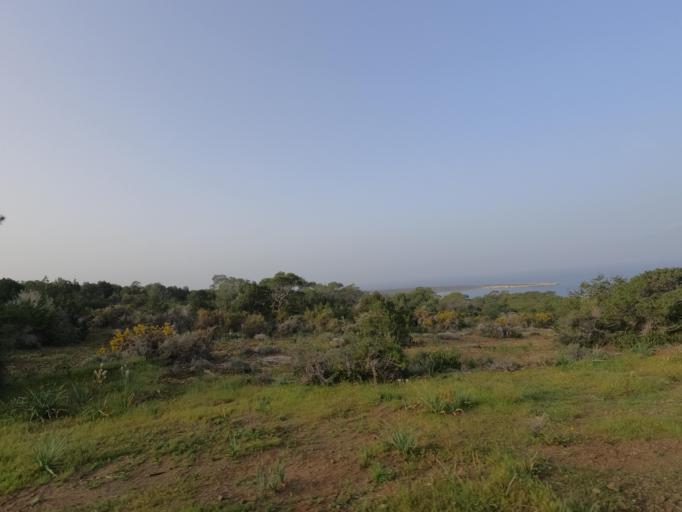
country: CY
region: Pafos
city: Pegeia
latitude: 34.9684
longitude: 32.3204
